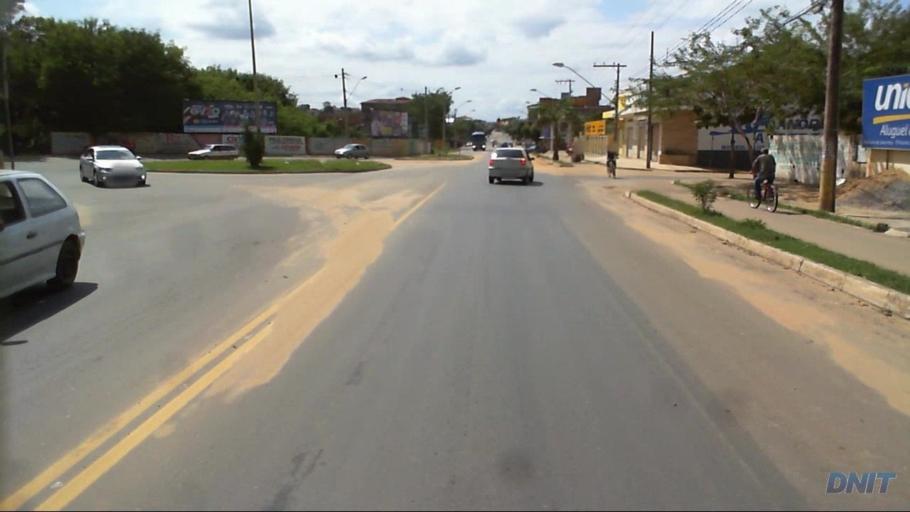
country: BR
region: Minas Gerais
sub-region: Governador Valadares
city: Governador Valadares
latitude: -18.8856
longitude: -41.9694
